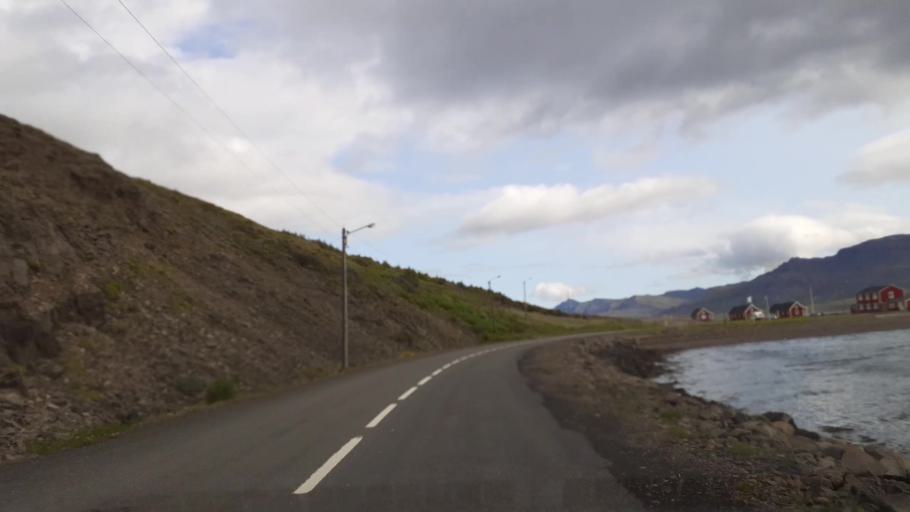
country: IS
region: East
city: Eskifjoerdur
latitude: 65.0622
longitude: -13.9934
